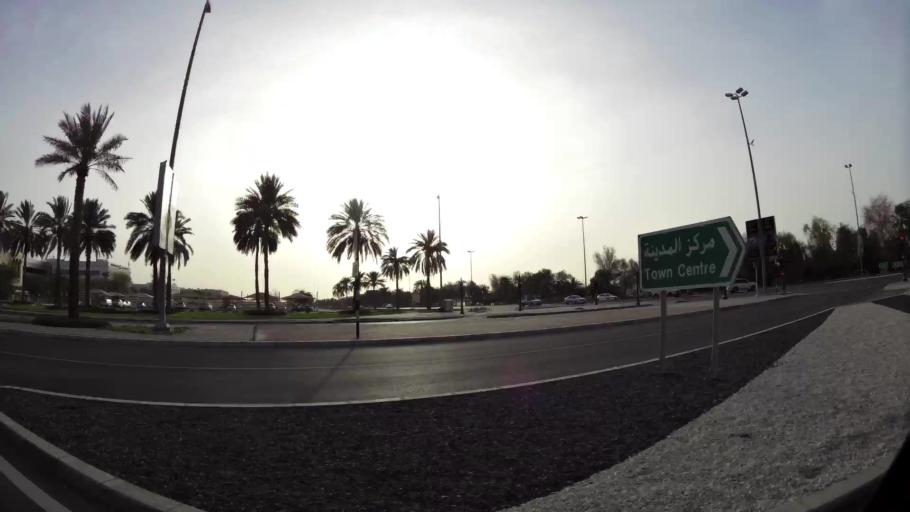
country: AE
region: Abu Dhabi
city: Al Ain
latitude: 24.2412
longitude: 55.7358
